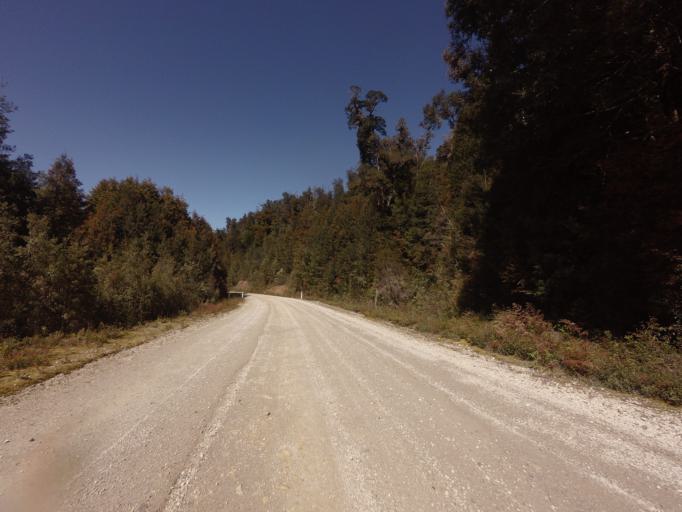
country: AU
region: Tasmania
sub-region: Huon Valley
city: Geeveston
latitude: -42.8407
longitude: 146.3759
